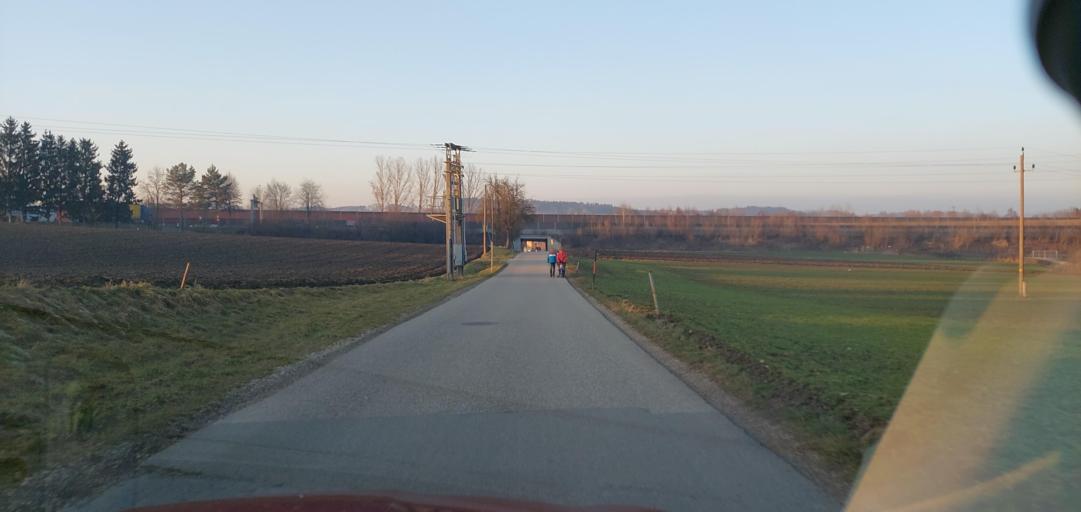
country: AT
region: Upper Austria
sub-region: Politischer Bezirk Grieskirchen
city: Bad Schallerbach
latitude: 48.1847
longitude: 13.9155
